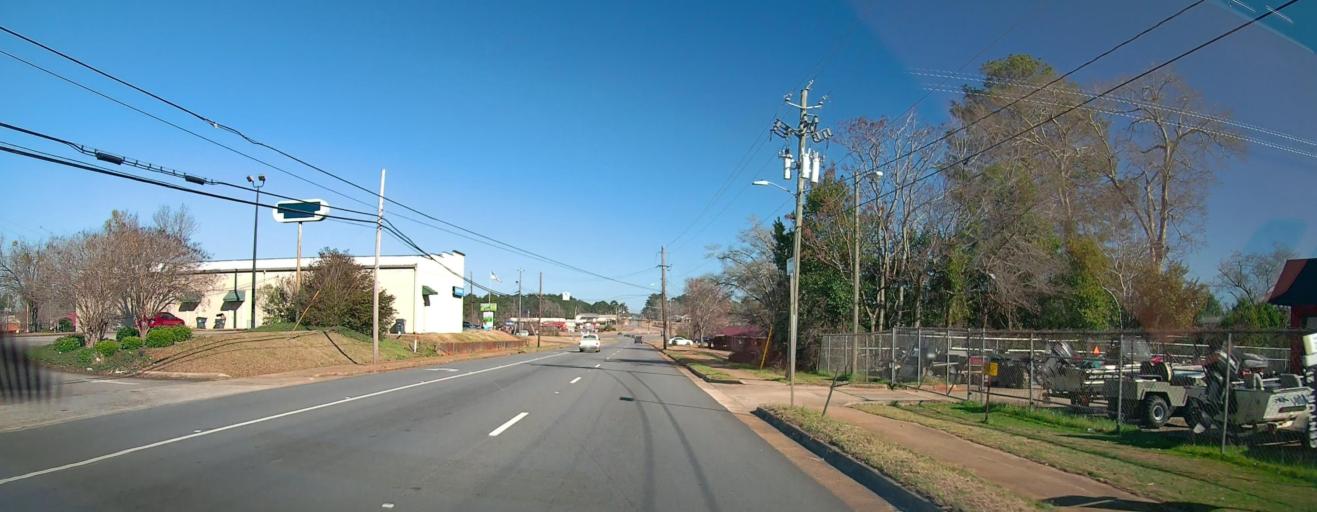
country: US
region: Georgia
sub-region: Sumter County
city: Americus
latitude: 32.0712
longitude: -84.2138
